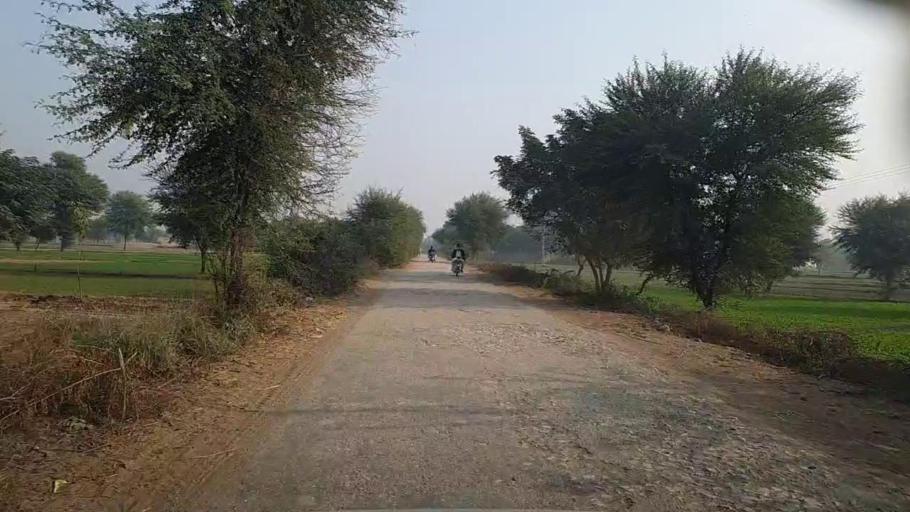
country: PK
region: Sindh
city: Kandiari
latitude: 27.0347
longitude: 68.4832
